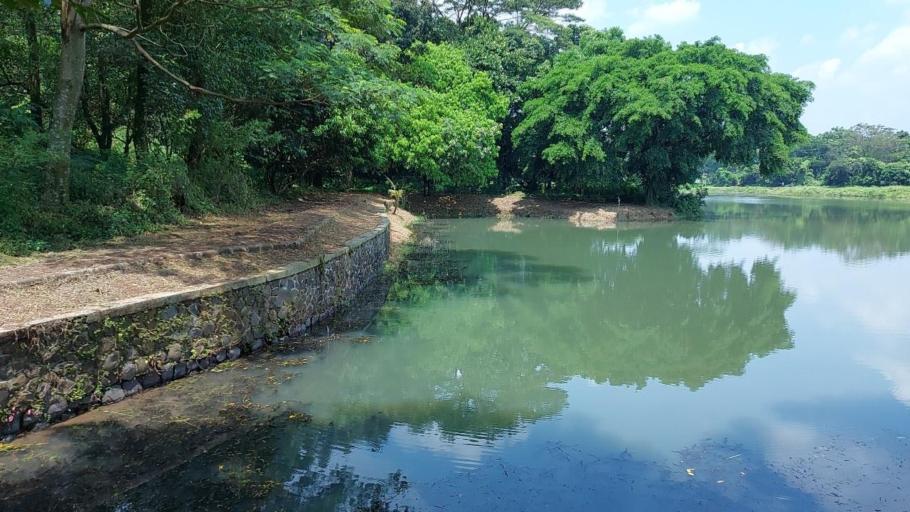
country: ID
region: West Java
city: Cibinong
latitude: -6.4903
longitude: 106.8523
